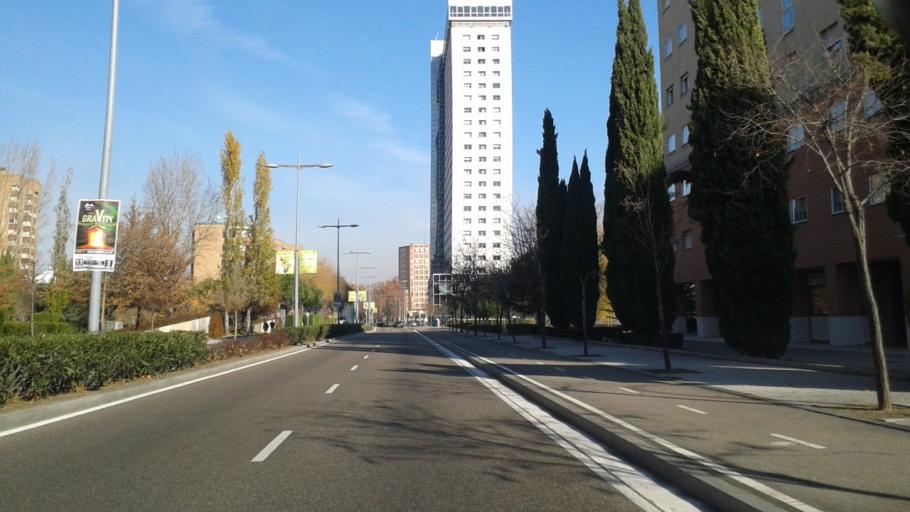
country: ES
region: Castille and Leon
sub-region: Provincia de Valladolid
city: Valladolid
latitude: 41.6571
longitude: -4.7355
